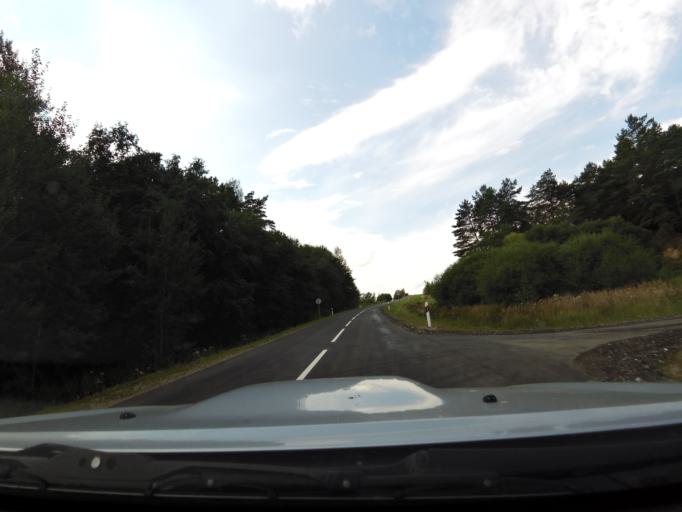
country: LT
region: Vilnius County
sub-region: Vilniaus Rajonas
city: Vievis
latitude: 54.8954
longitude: 24.7715
